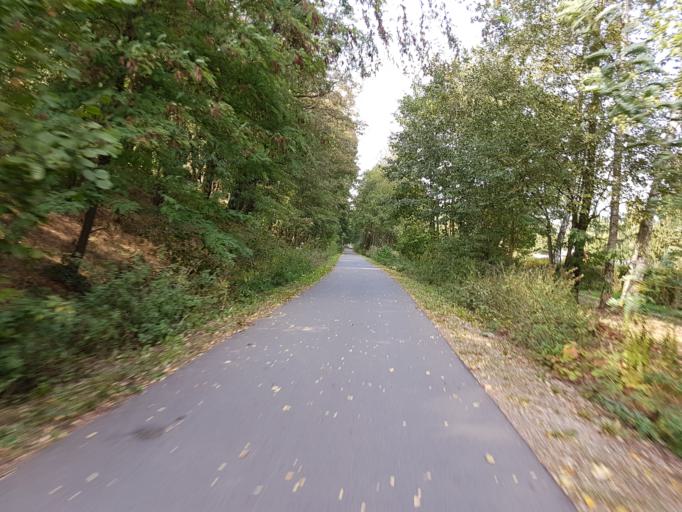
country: DE
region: Saxony
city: Claussnitz
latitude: 50.9081
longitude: 12.8970
